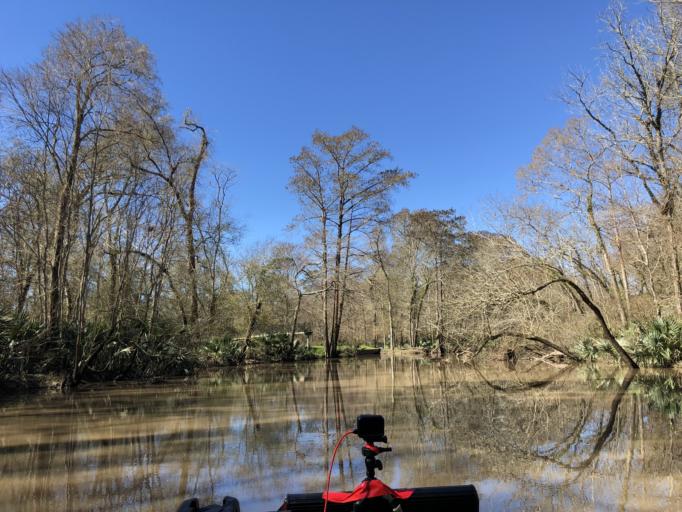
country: US
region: Louisiana
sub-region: Calcasieu Parish
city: Iowa
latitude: 30.3148
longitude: -93.0756
